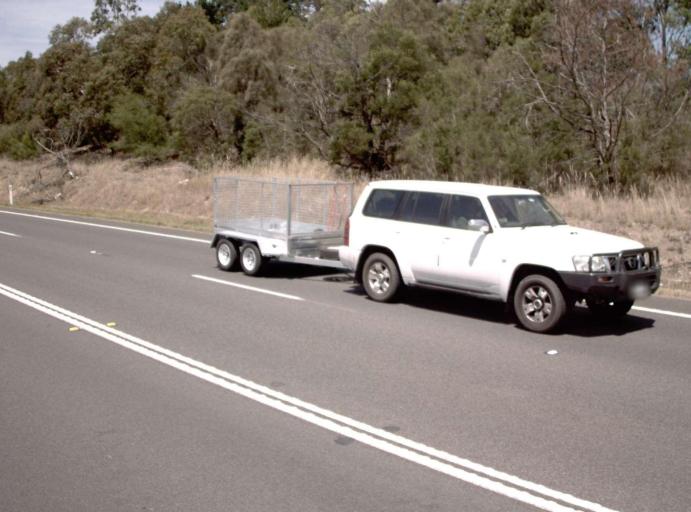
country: AU
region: Victoria
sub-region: Latrobe
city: Traralgon
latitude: -38.1715
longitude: 146.6736
